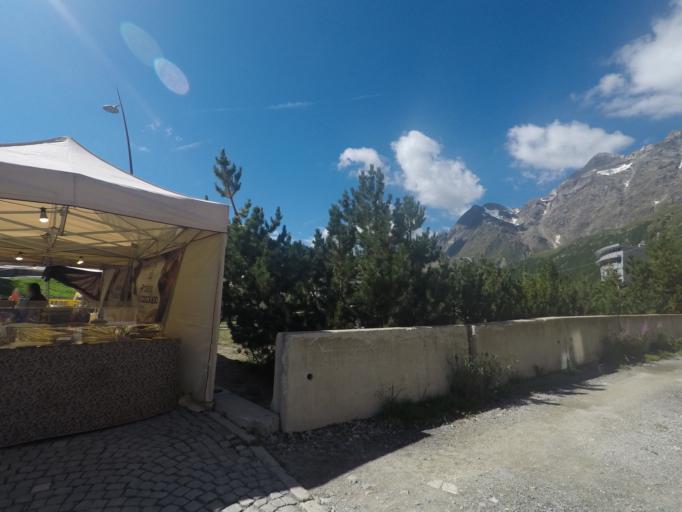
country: IT
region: Aosta Valley
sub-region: Valle d'Aosta
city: Paquier
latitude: 45.9348
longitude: 7.6308
